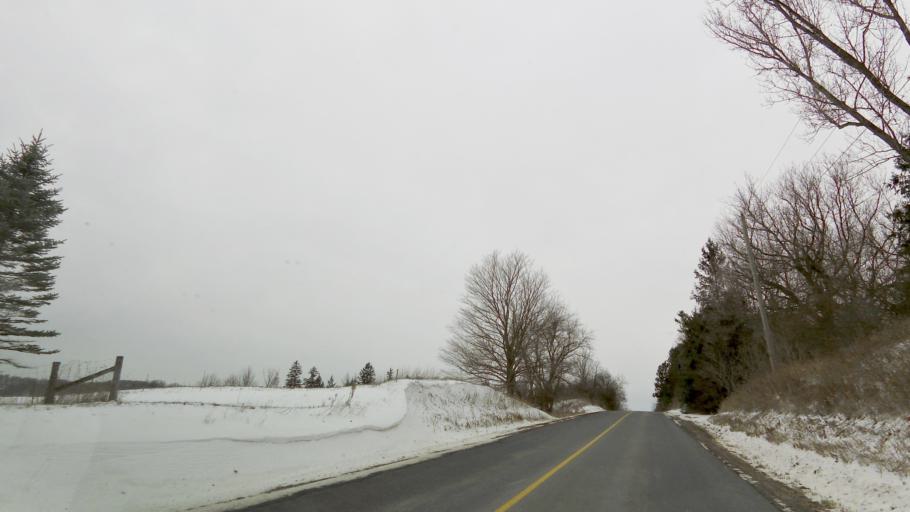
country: CA
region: Ontario
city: Bradford West Gwillimbury
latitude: 43.9514
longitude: -79.6388
